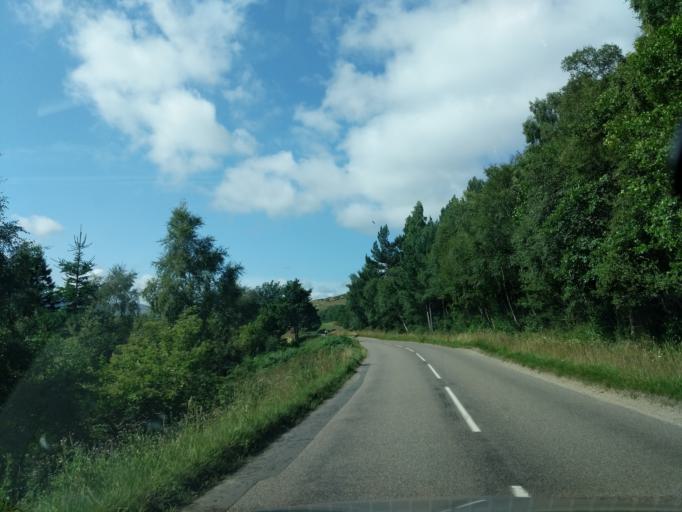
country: GB
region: Scotland
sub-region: Moray
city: Dufftown
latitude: 57.4149
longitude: -3.1660
